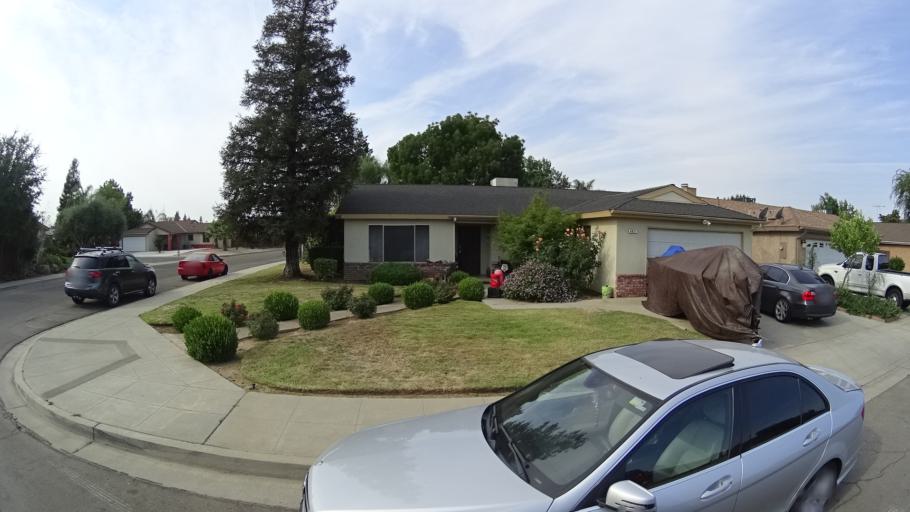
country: US
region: California
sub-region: Fresno County
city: West Park
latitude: 36.7751
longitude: -119.8729
